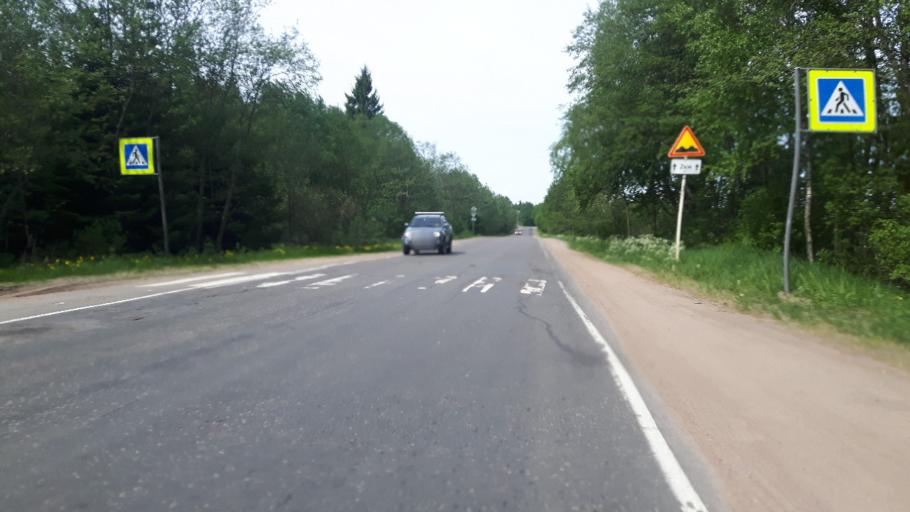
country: RU
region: Leningrad
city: Ust'-Luga
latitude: 59.6377
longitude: 28.2859
